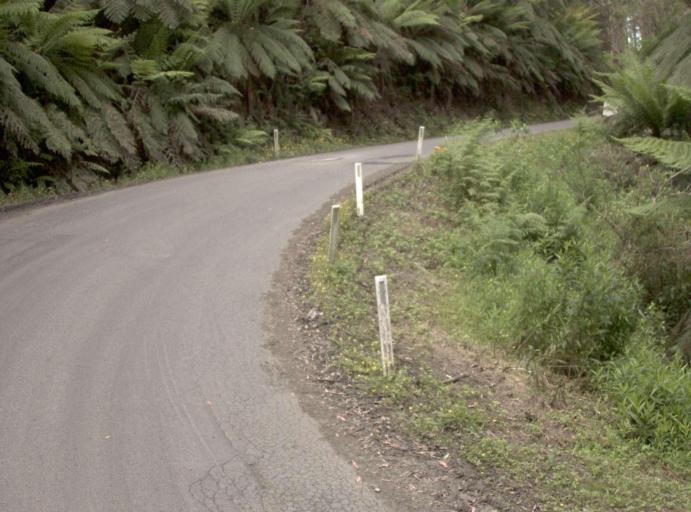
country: AU
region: Victoria
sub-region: Latrobe
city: Traralgon
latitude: -38.4220
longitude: 146.5700
